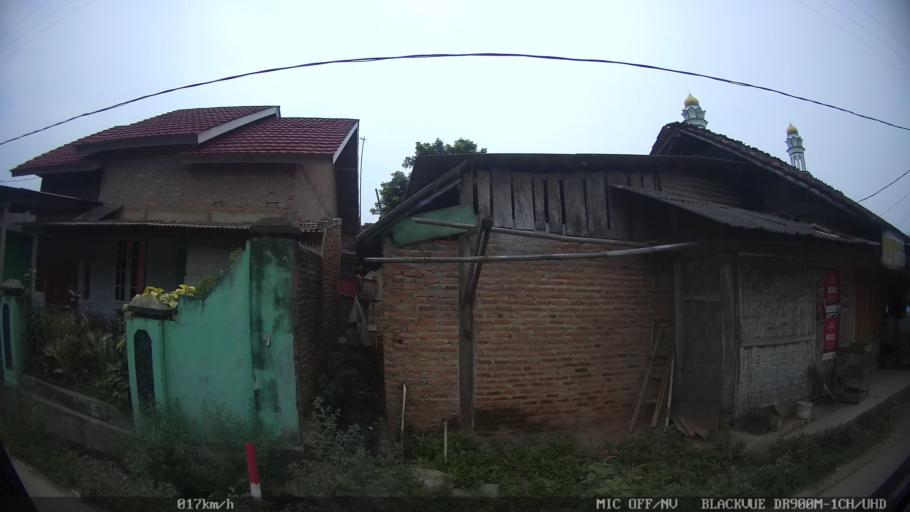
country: ID
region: Lampung
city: Panjang
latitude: -5.4147
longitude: 105.3466
